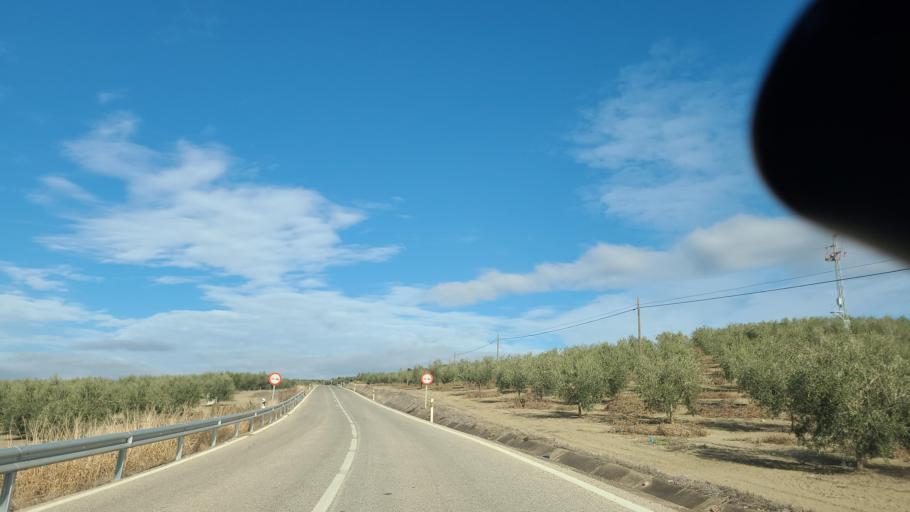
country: ES
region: Andalusia
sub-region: Provincia de Jaen
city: Espeluy
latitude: 38.0159
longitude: -3.8839
